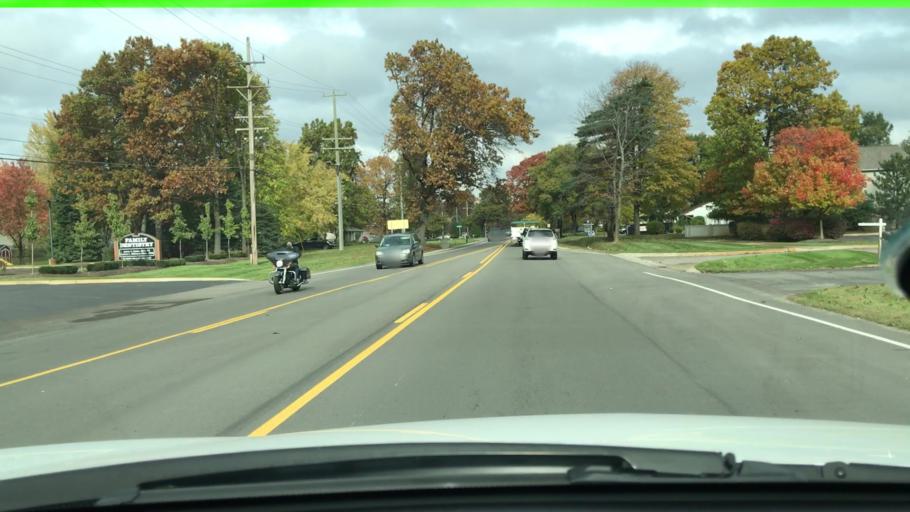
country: US
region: Michigan
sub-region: Oakland County
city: Waterford
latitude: 42.6451
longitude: -83.4433
